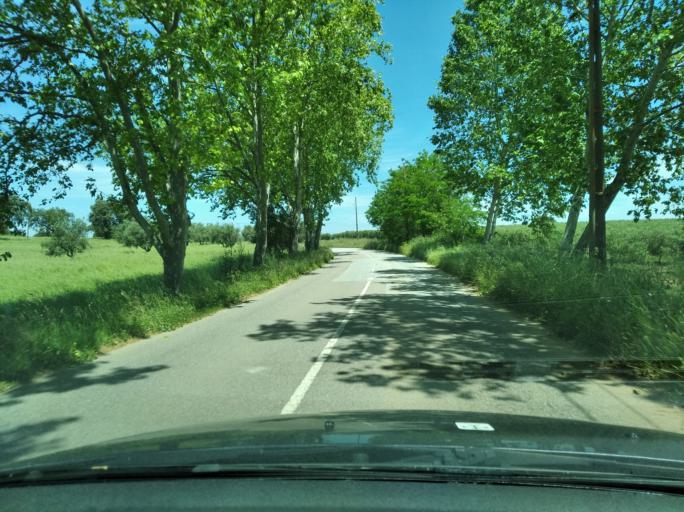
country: PT
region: Portalegre
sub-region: Avis
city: Avis
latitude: 39.0950
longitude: -7.8788
